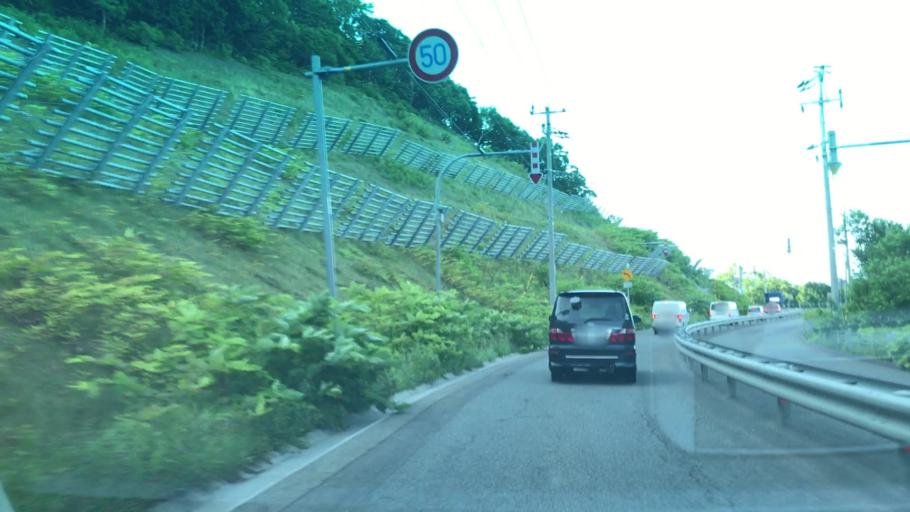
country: JP
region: Hokkaido
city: Otaru
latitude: 43.1384
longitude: 141.0139
